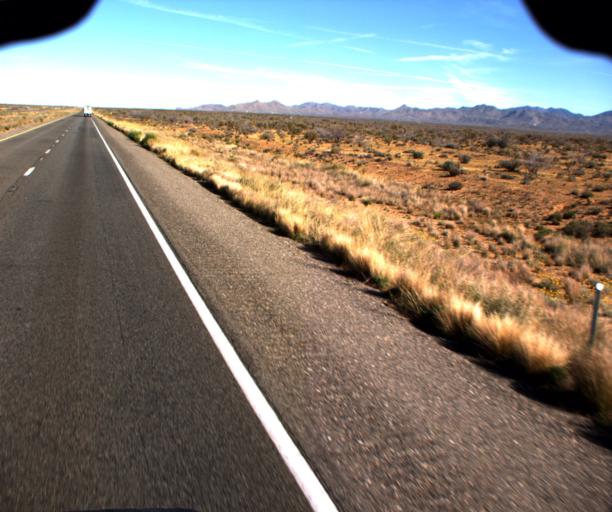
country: US
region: Arizona
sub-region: Mohave County
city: Golden Valley
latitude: 35.3377
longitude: -114.2163
